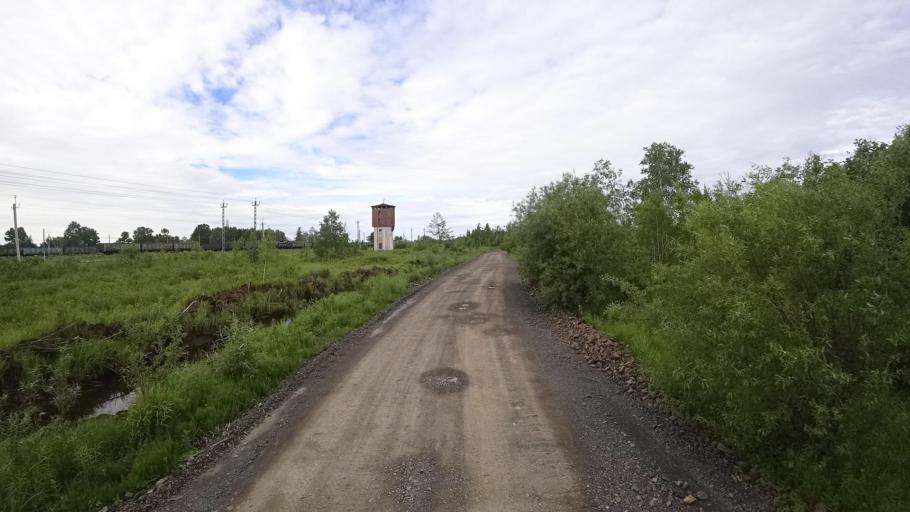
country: RU
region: Khabarovsk Krai
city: Amursk
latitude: 49.9014
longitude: 136.1367
